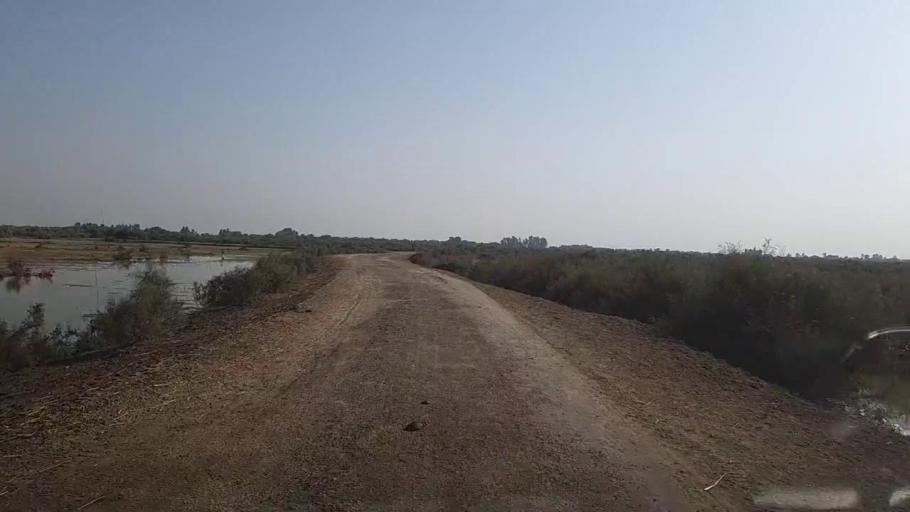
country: PK
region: Sindh
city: Kandhkot
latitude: 28.3608
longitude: 69.3303
